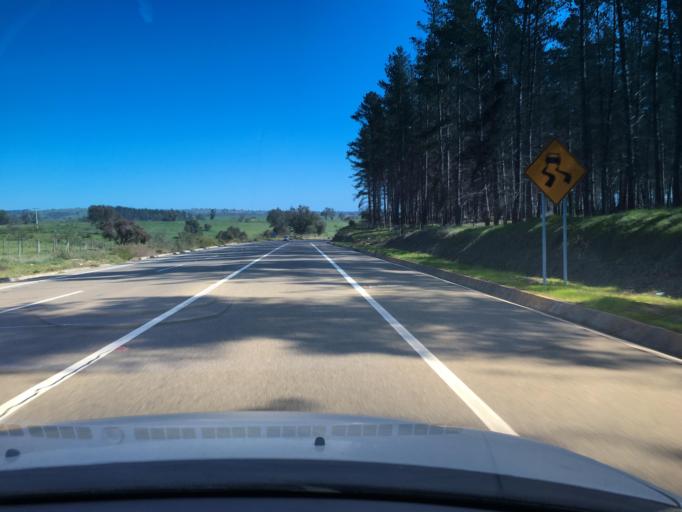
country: CL
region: Valparaiso
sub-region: San Antonio Province
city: El Tabo
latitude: -33.4089
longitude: -71.5114
